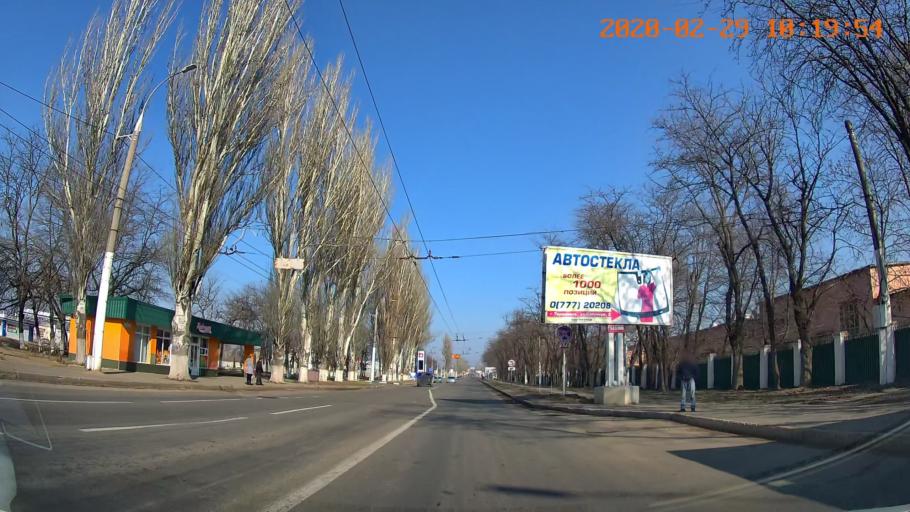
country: MD
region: Telenesti
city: Tiraspolul Nou
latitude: 46.8556
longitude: 29.6116
